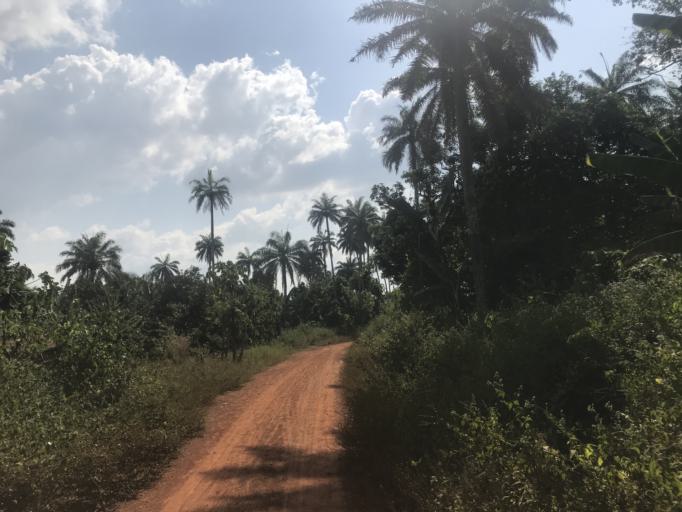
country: NG
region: Osun
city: Ibokun
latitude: 7.8217
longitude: 4.7002
